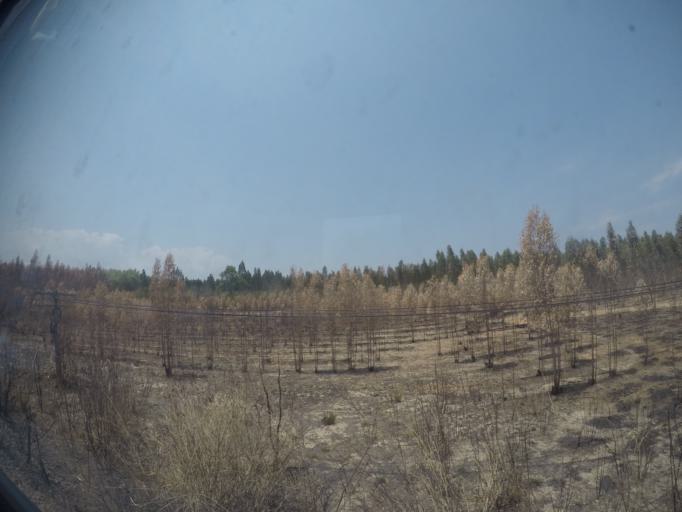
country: VN
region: Binh Thuan
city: Thuan Nam
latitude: 10.9287
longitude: 107.9138
